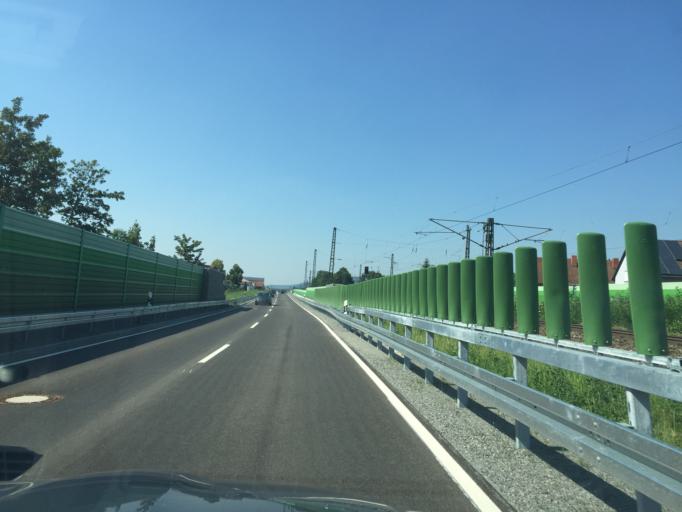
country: DE
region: Baden-Wuerttemberg
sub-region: Karlsruhe Region
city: Hemsbach
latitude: 49.5927
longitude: 8.6481
